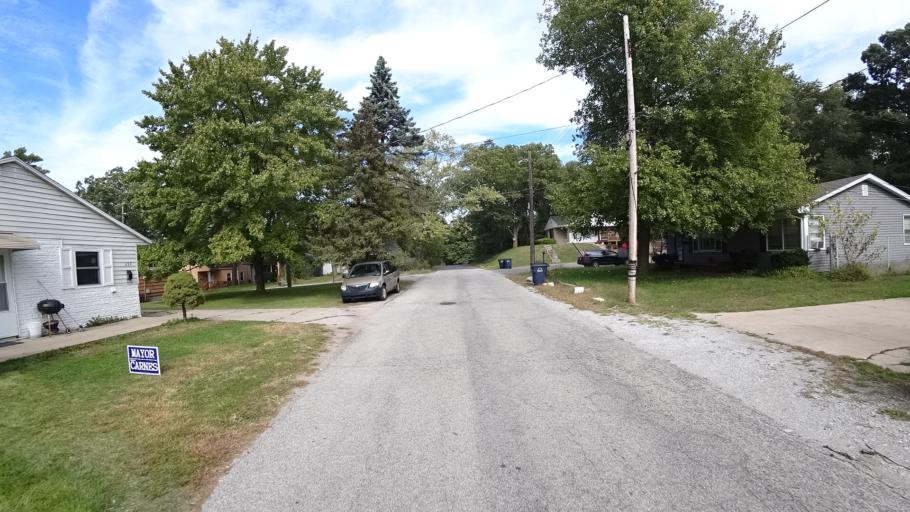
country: US
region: Indiana
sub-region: LaPorte County
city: Michigan City
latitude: 41.7159
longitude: -86.8776
